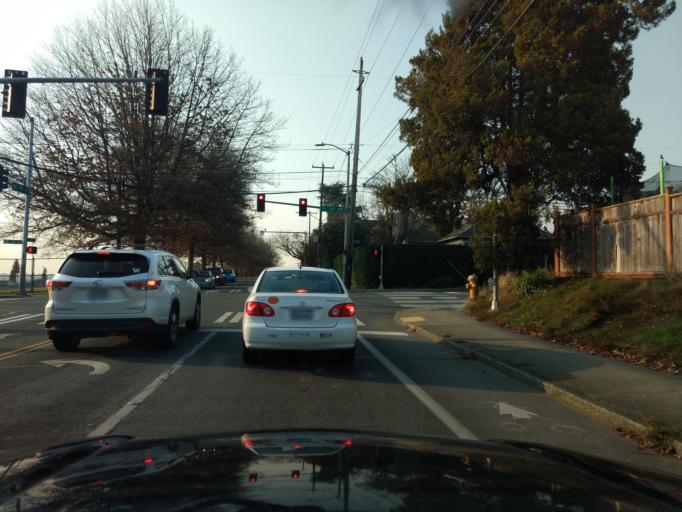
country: US
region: Washington
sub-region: King County
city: Shoreline
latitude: 47.6831
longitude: -122.3118
